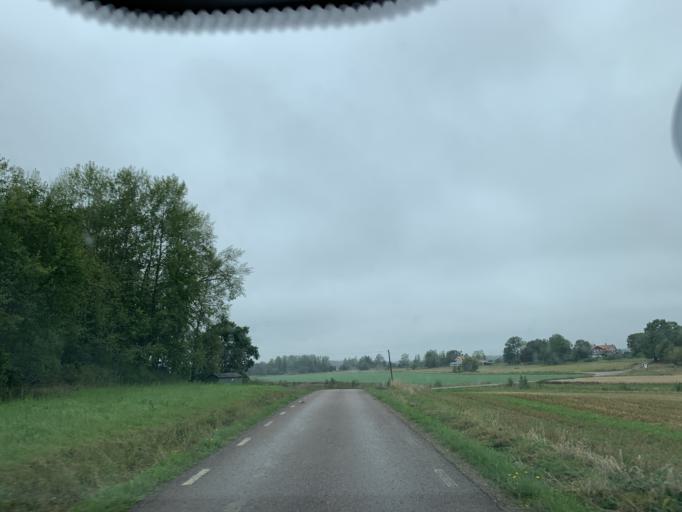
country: SE
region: Soedermanland
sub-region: Eskilstuna Kommun
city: Kvicksund
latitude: 59.5463
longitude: 16.3589
